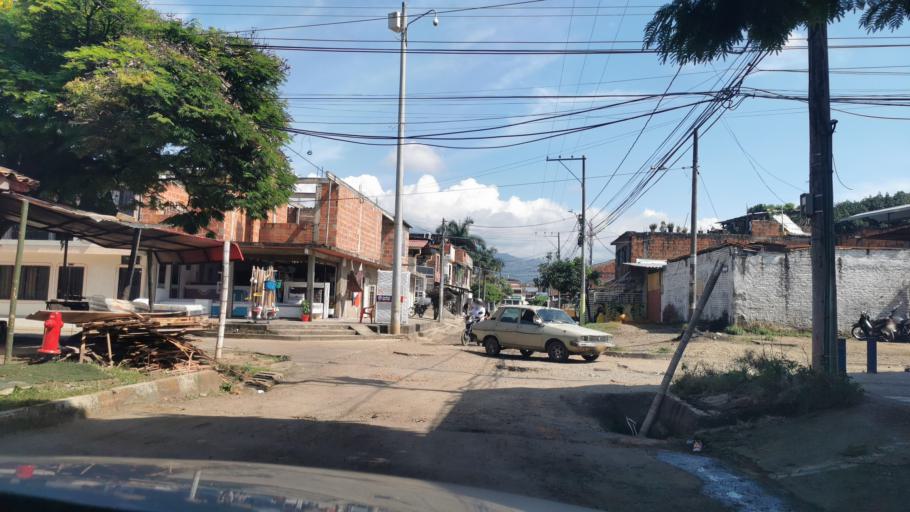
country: CO
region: Valle del Cauca
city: Jamundi
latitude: 3.2628
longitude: -76.5364
